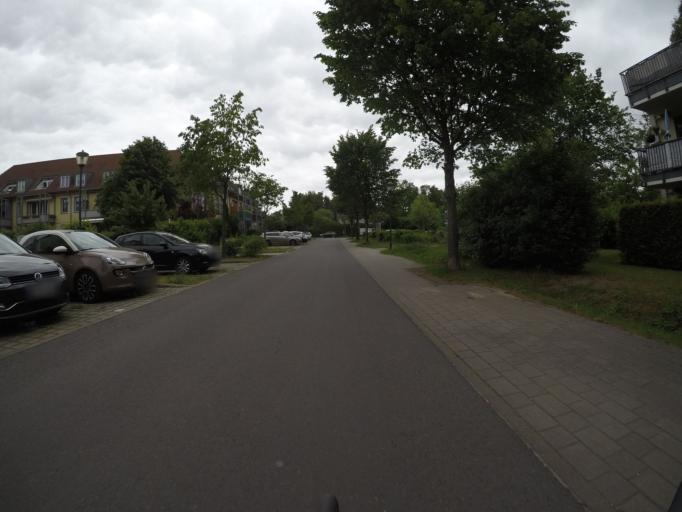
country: DE
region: Brandenburg
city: Glienicke
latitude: 52.6372
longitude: 13.3211
